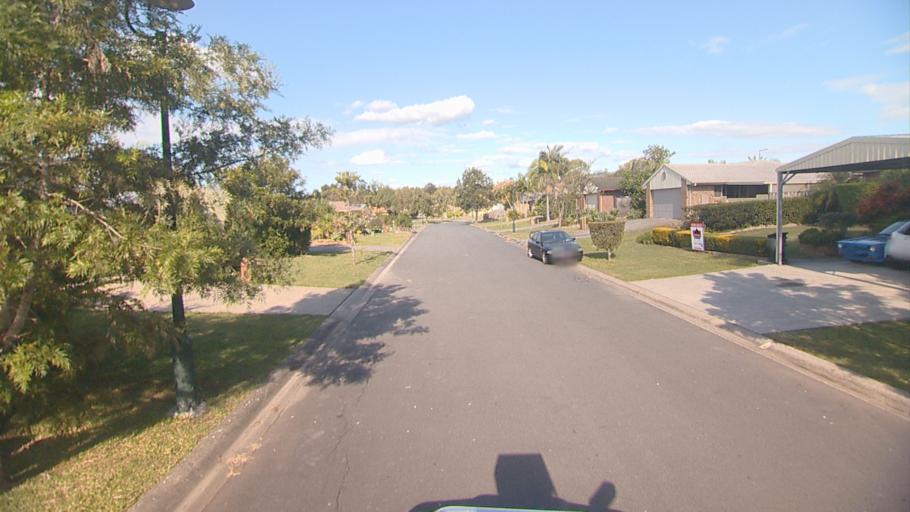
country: AU
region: Queensland
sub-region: Logan
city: Windaroo
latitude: -27.7506
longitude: 153.1949
